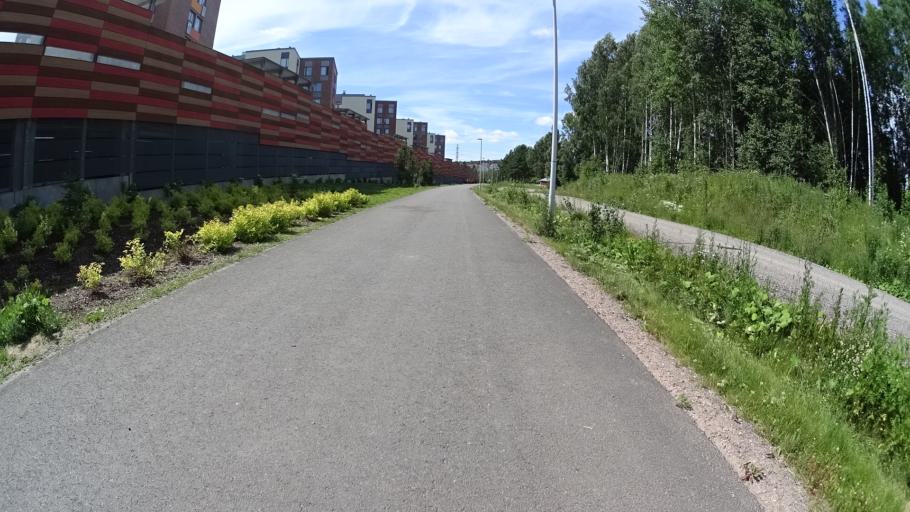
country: FI
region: Uusimaa
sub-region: Helsinki
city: Teekkarikylae
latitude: 60.2554
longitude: 24.8687
